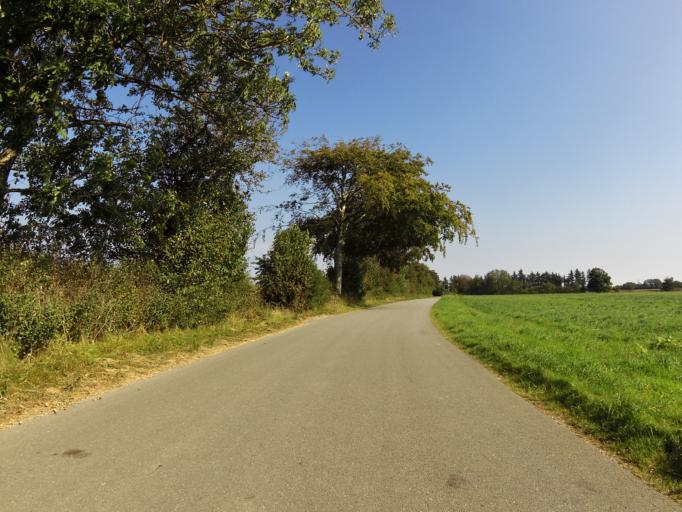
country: DK
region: South Denmark
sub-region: Vejen Kommune
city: Rodding
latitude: 55.3715
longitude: 9.1325
